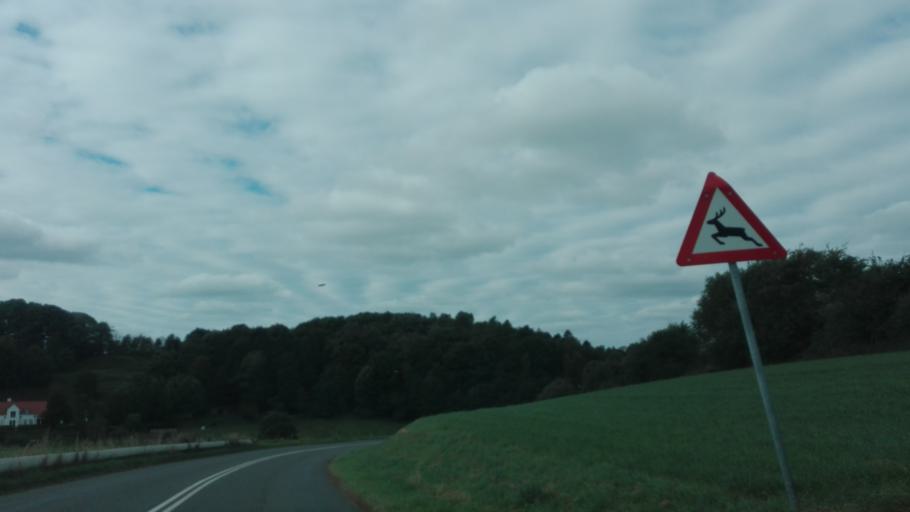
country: DK
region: Central Jutland
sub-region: Skanderborg Kommune
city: Stilling
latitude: 56.0831
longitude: 9.9928
